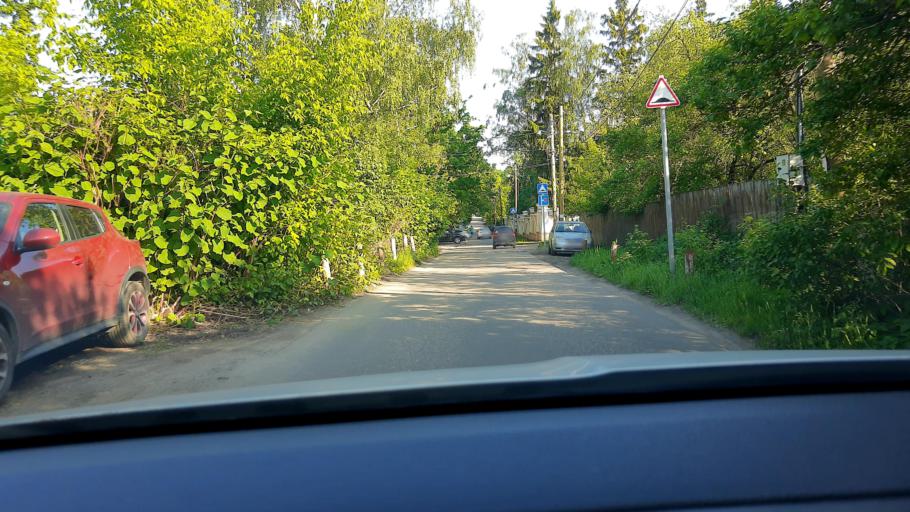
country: RU
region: Moscow
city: Mikhalkovo
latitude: 55.6782
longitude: 37.4146
